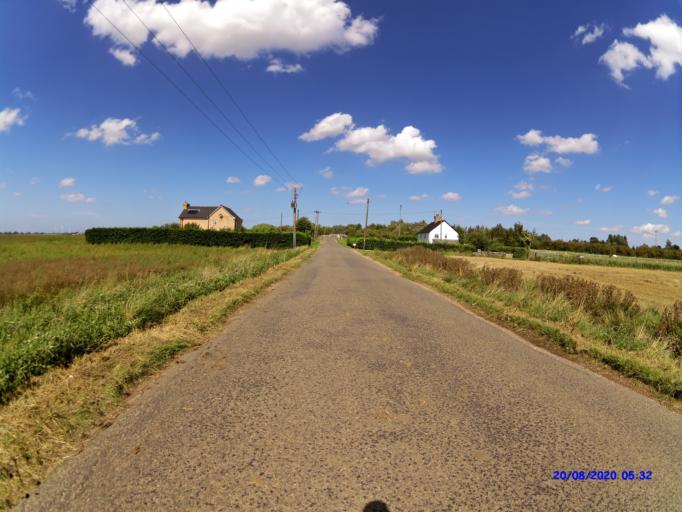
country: GB
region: England
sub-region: Cambridgeshire
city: Whittlesey
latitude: 52.5423
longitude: -0.1101
